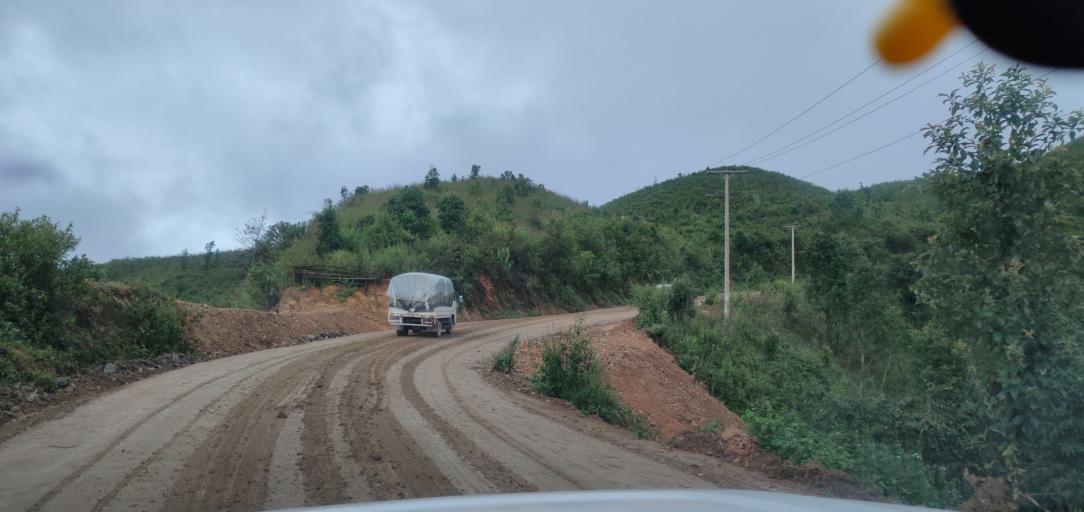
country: LA
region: Phongsali
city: Phongsali
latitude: 21.4228
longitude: 102.1714
